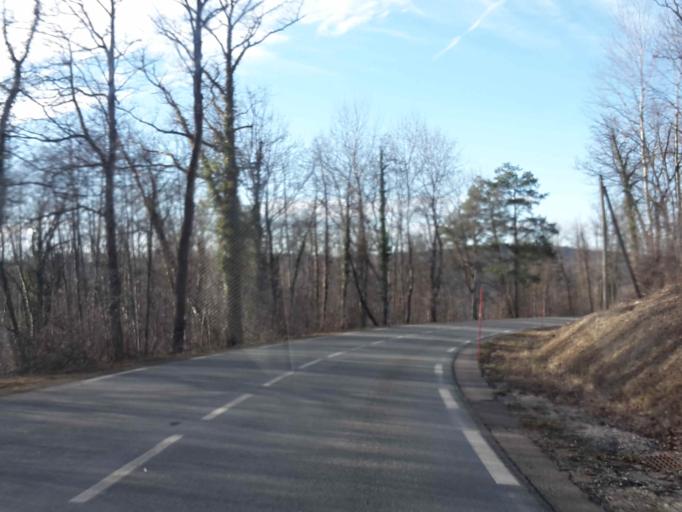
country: FR
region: Franche-Comte
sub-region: Departement du Doubs
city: Vercel-Villedieu-le-Camp
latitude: 47.2202
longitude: 6.3923
